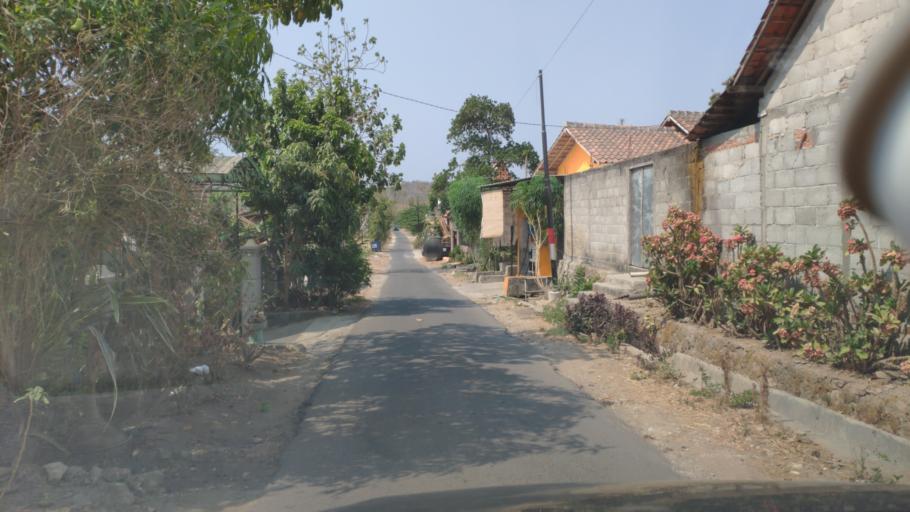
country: ID
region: Central Java
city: Tempuran
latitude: -6.9143
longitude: 111.4552
